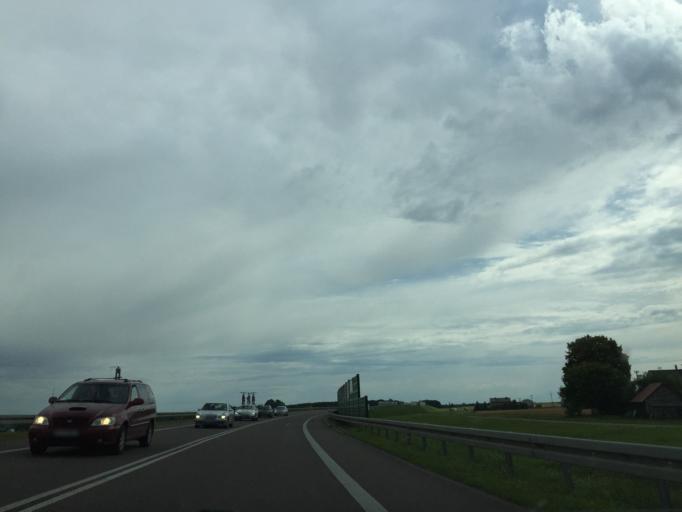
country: PL
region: Lublin Voivodeship
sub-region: Powiat bialski
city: Rzeczyca
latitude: 51.9926
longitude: 22.7521
